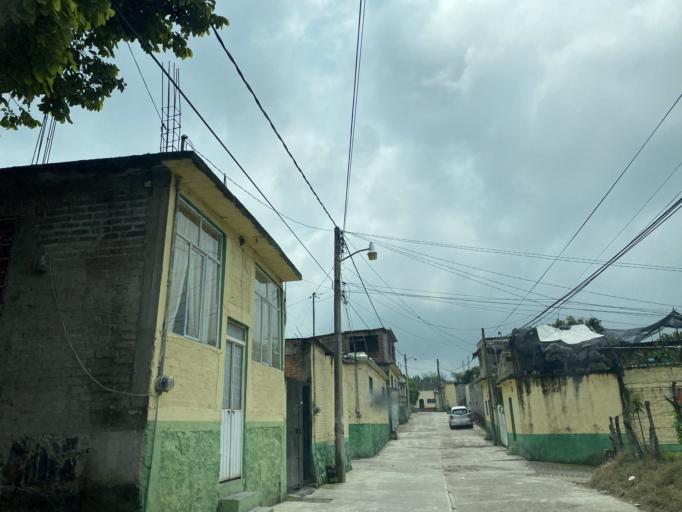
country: MX
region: Morelos
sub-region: Yecapixtla
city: Achichipico
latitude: 18.9477
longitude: -98.8257
